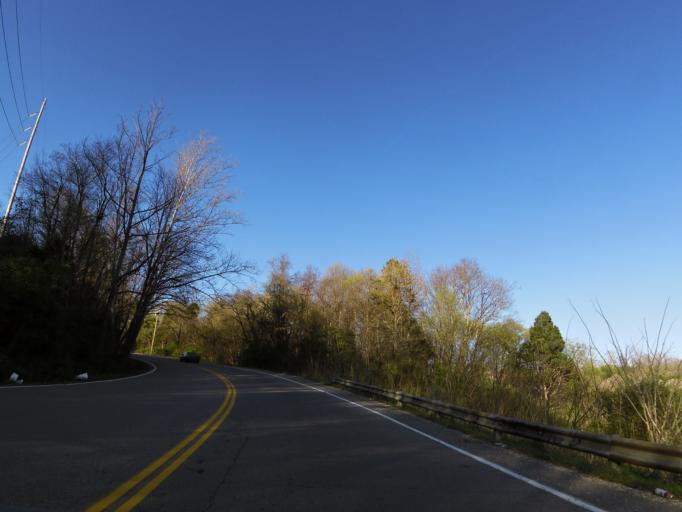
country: US
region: Tennessee
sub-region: Knox County
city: Knoxville
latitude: 35.9479
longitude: -83.8245
